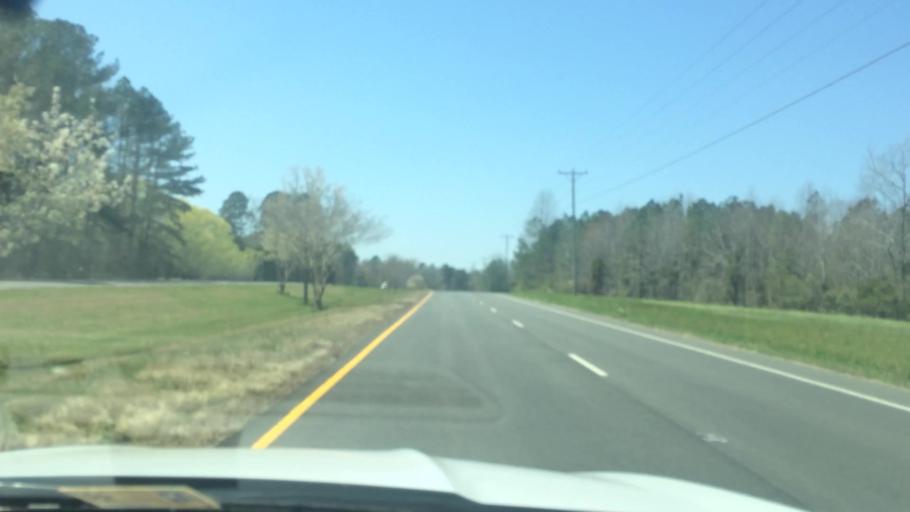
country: US
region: Virginia
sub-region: Middlesex County
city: Saluda
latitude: 37.5995
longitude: -76.5770
